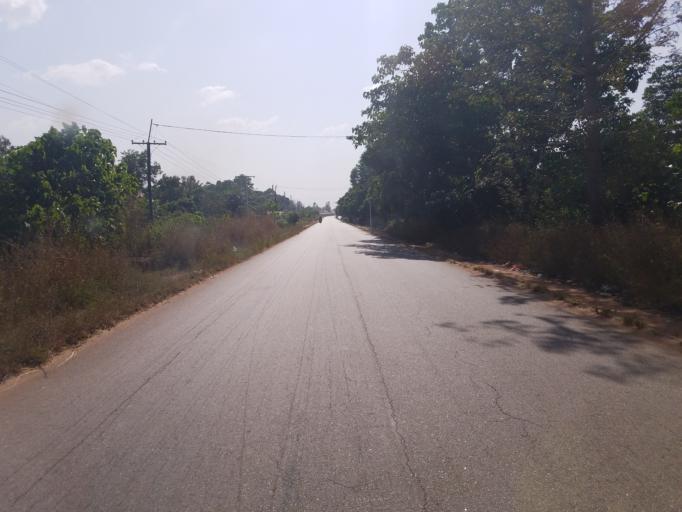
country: GN
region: Boke
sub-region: Fria
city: Fria
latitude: 10.0791
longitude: -13.6996
